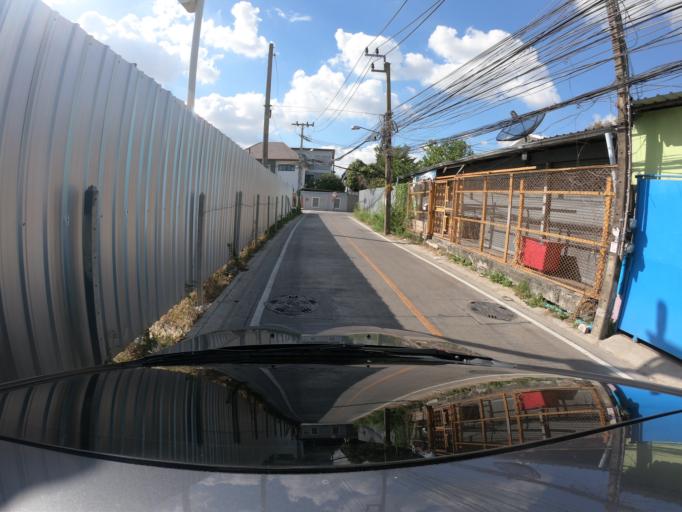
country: TH
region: Bangkok
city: Bang Na
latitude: 13.6471
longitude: 100.6243
